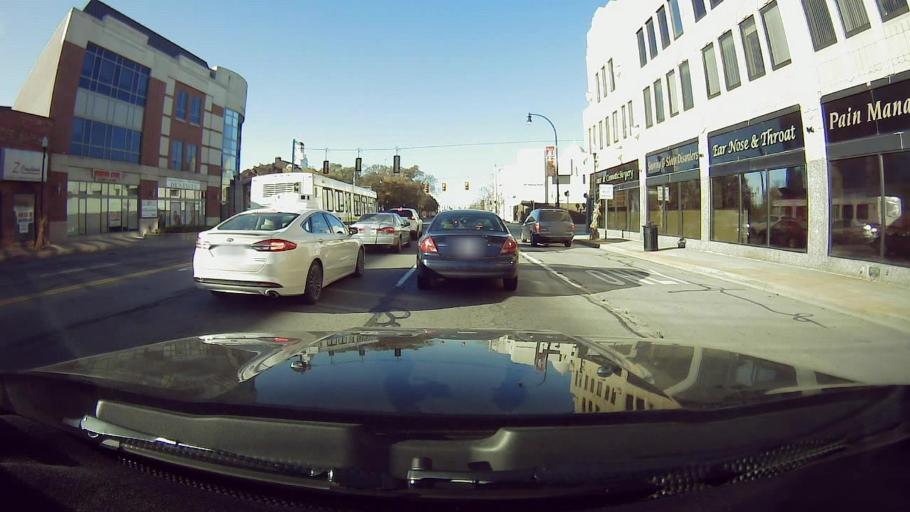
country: US
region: Michigan
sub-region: Wayne County
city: Dearborn
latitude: 42.3225
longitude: -83.1750
